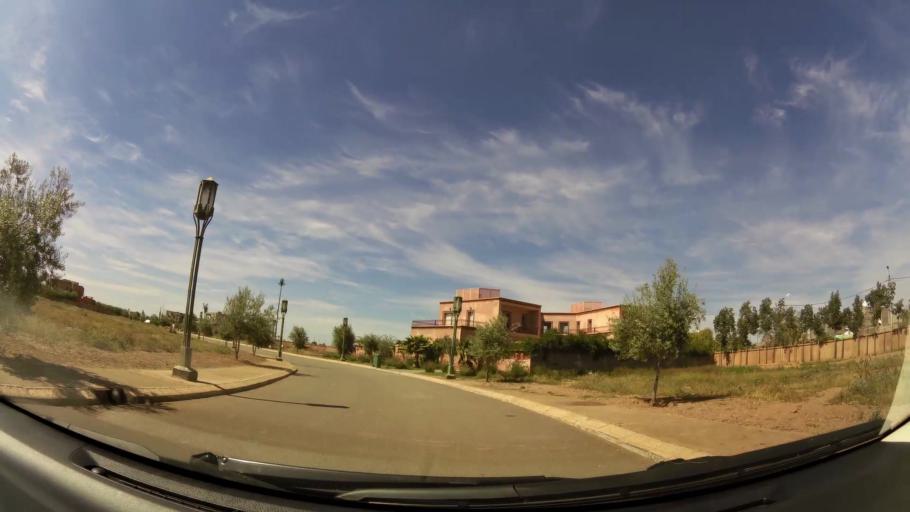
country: MA
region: Marrakech-Tensift-Al Haouz
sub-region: Marrakech
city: Marrakesh
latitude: 31.6201
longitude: -7.9219
